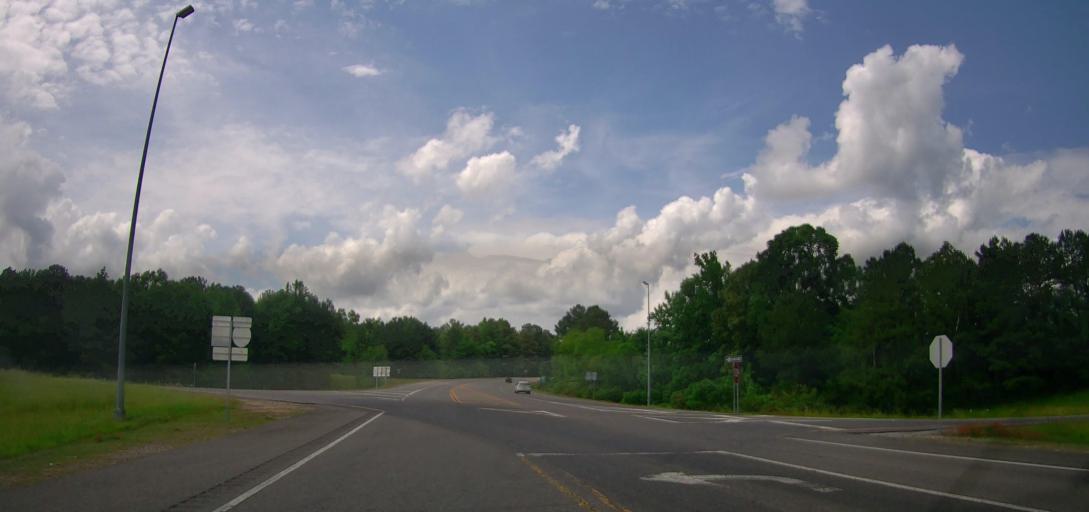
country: US
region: Alabama
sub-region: Marion County
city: Hamilton
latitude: 34.0728
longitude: -87.9762
